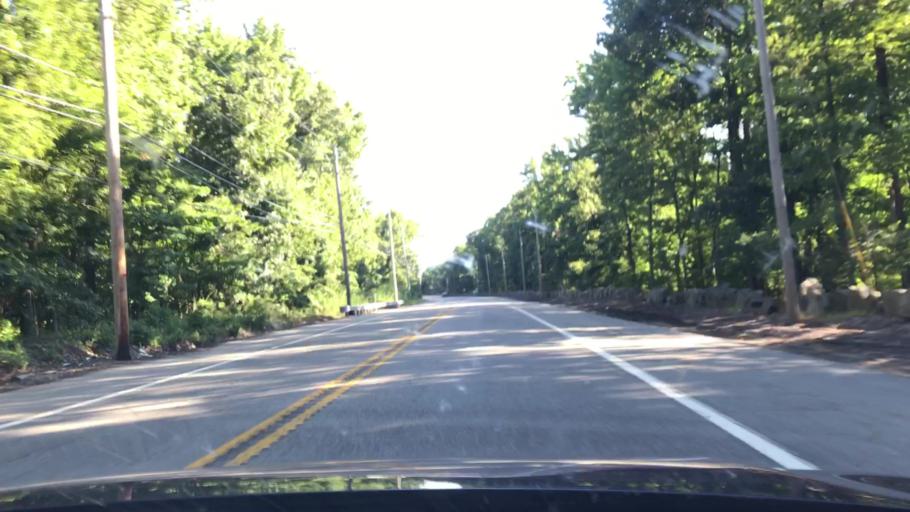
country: US
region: New Jersey
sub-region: Bergen County
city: Alpine
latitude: 40.9690
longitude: -73.9170
